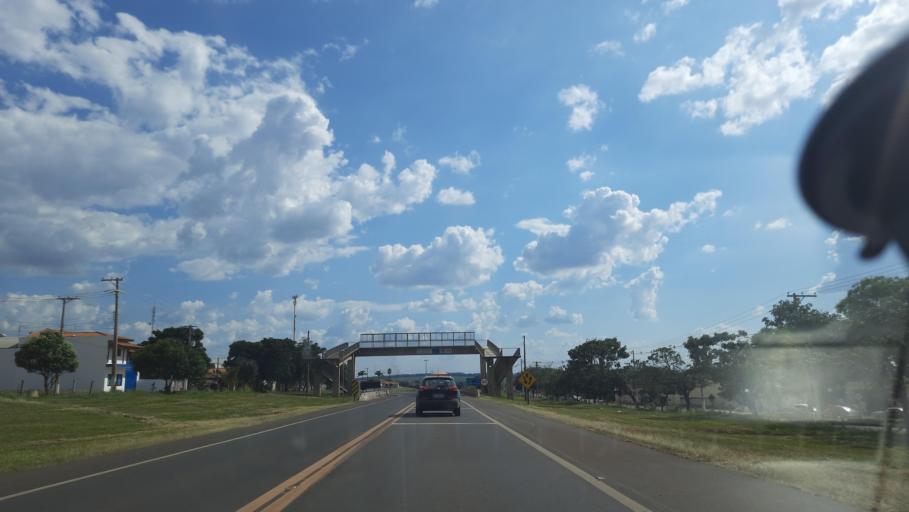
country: BR
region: Sao Paulo
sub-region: Casa Branca
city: Casa Branca
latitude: -21.7337
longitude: -46.9699
